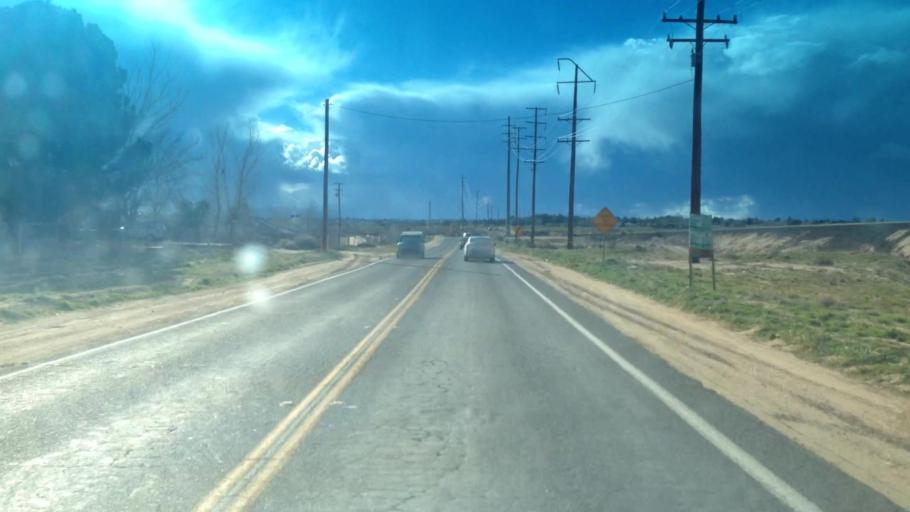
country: US
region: California
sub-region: San Bernardino County
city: Hesperia
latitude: 34.4142
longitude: -117.2287
